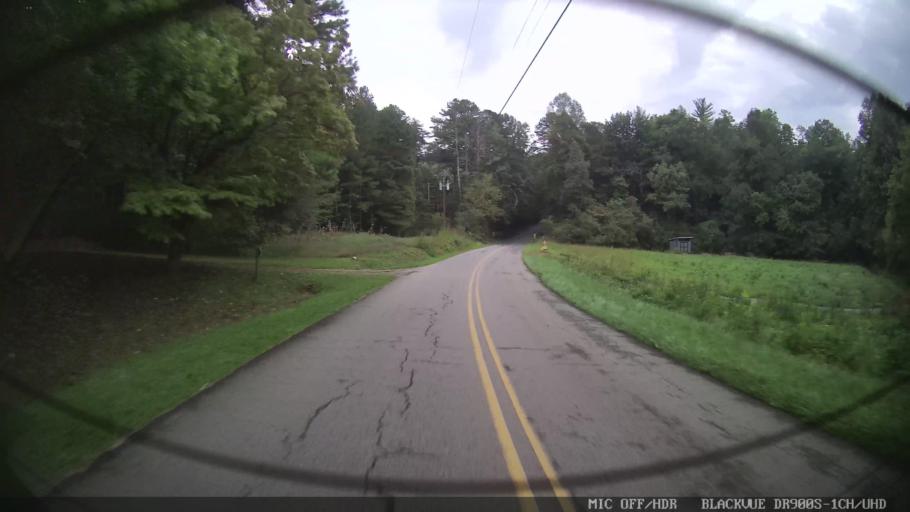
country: US
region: Georgia
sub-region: Gilmer County
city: Ellijay
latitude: 34.7543
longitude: -84.5278
